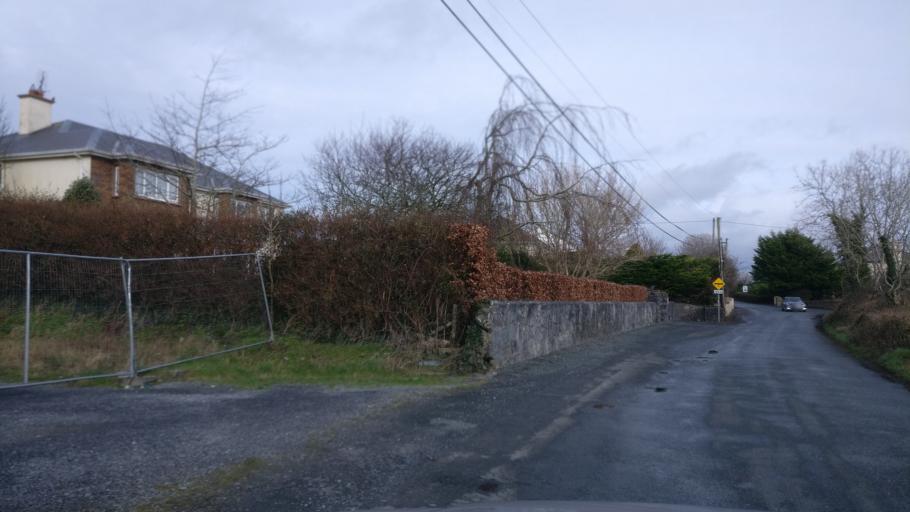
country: IE
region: Connaught
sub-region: County Galway
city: Oranmore
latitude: 53.2503
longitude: -8.9061
